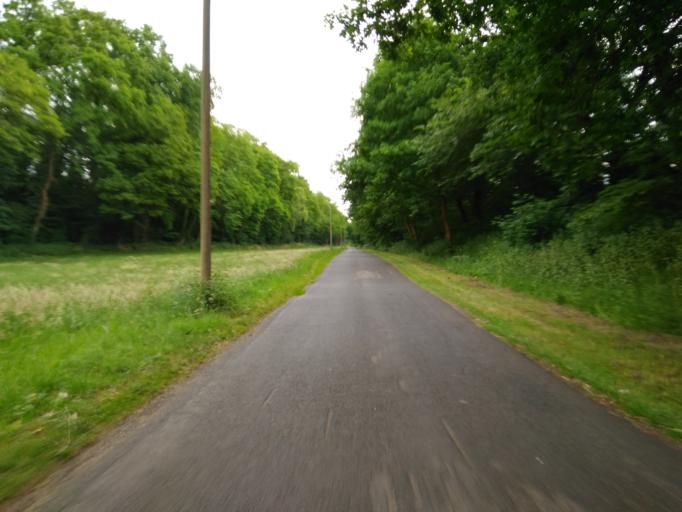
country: DE
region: North Rhine-Westphalia
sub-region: Regierungsbezirk Dusseldorf
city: Schermbeck
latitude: 51.6644
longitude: 6.9017
